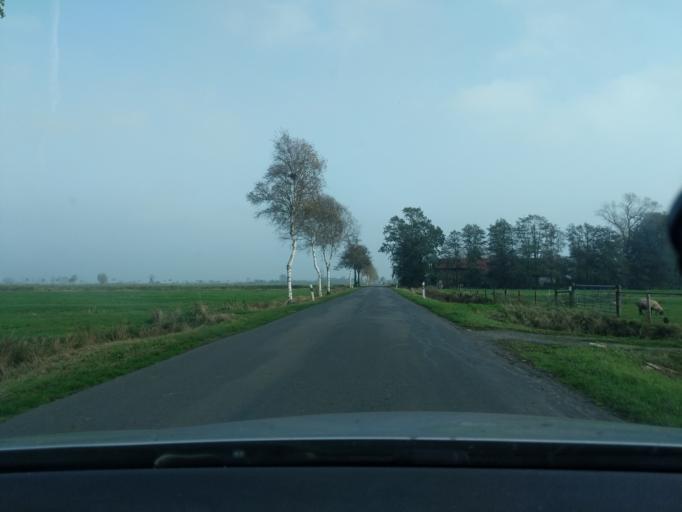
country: DE
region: Lower Saxony
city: Wanna
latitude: 53.7255
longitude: 8.7986
